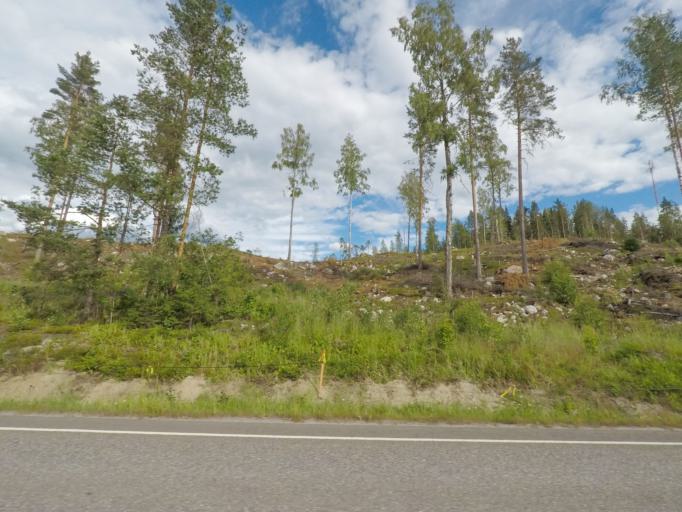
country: FI
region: Uusimaa
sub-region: Porvoo
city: Pukkila
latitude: 60.7988
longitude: 25.4718
